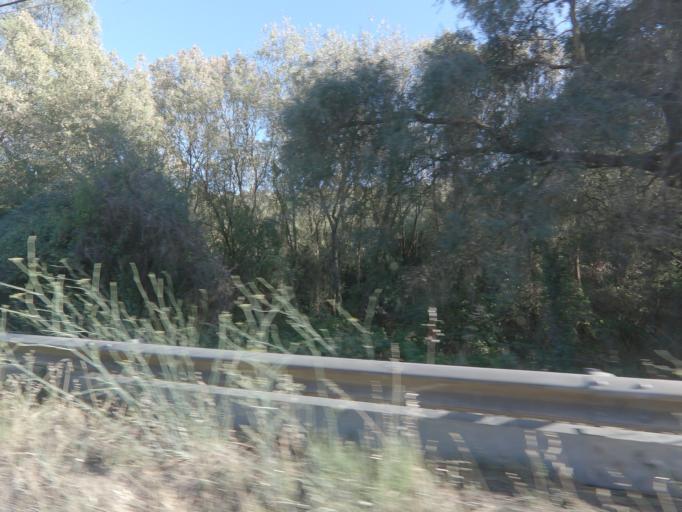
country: PT
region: Setubal
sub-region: Setubal
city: Setubal
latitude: 38.5034
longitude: -8.9435
